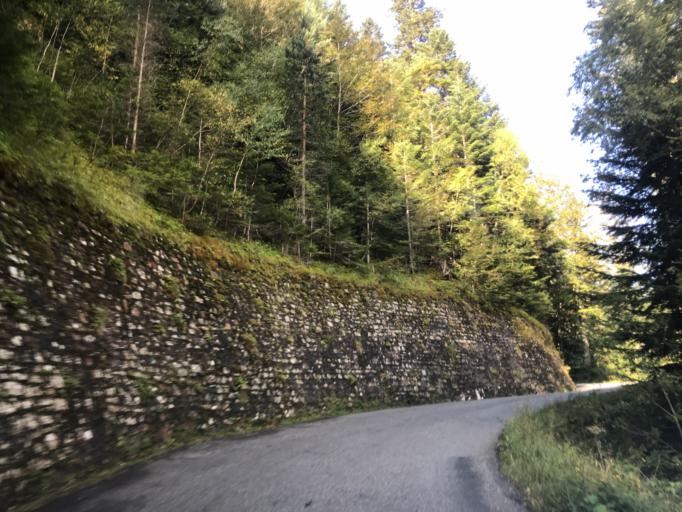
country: FR
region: Midi-Pyrenees
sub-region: Departement des Hautes-Pyrenees
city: Saint-Lary-Soulan
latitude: 42.8145
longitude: 0.2044
